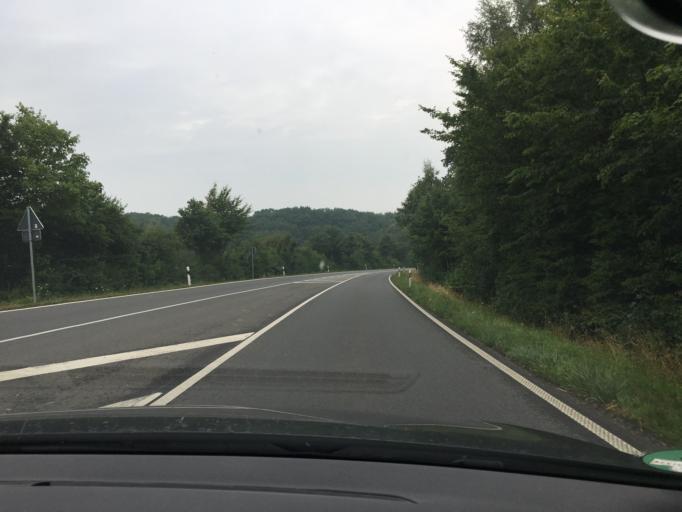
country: DE
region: North Rhine-Westphalia
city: Julich
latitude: 50.9268
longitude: 6.4108
